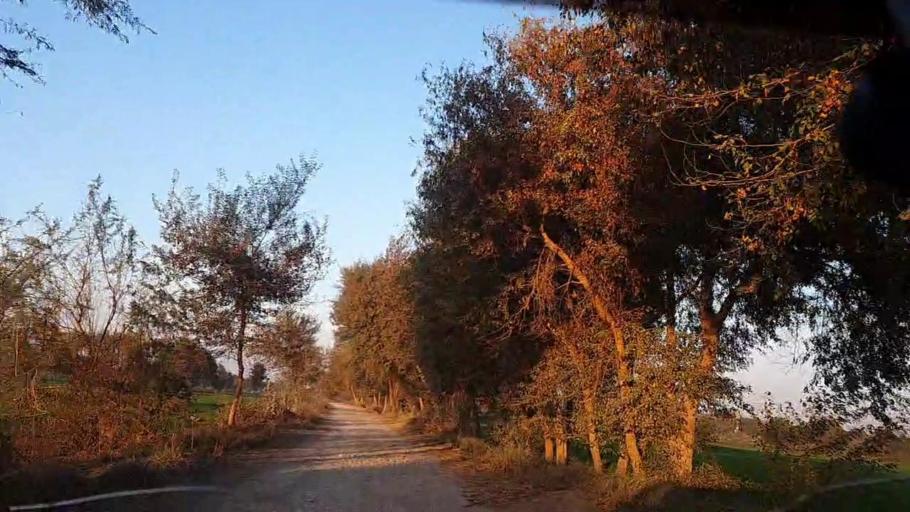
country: PK
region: Sindh
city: Adilpur
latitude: 27.8300
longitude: 69.2936
